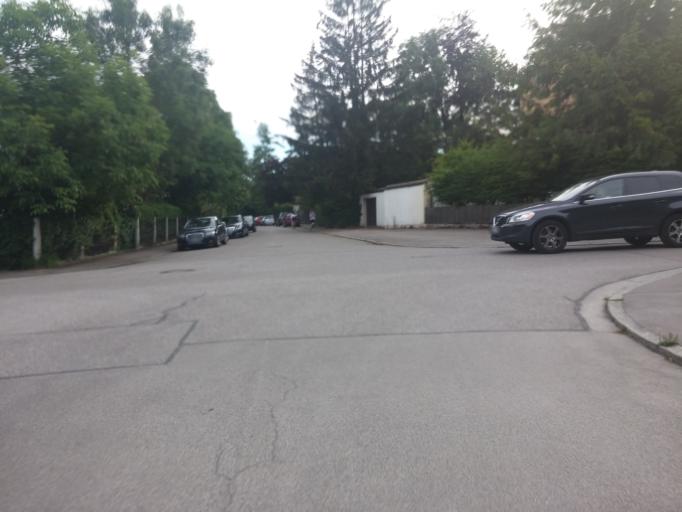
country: DE
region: Bavaria
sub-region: Upper Bavaria
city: Haar
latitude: 48.1104
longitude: 11.7047
